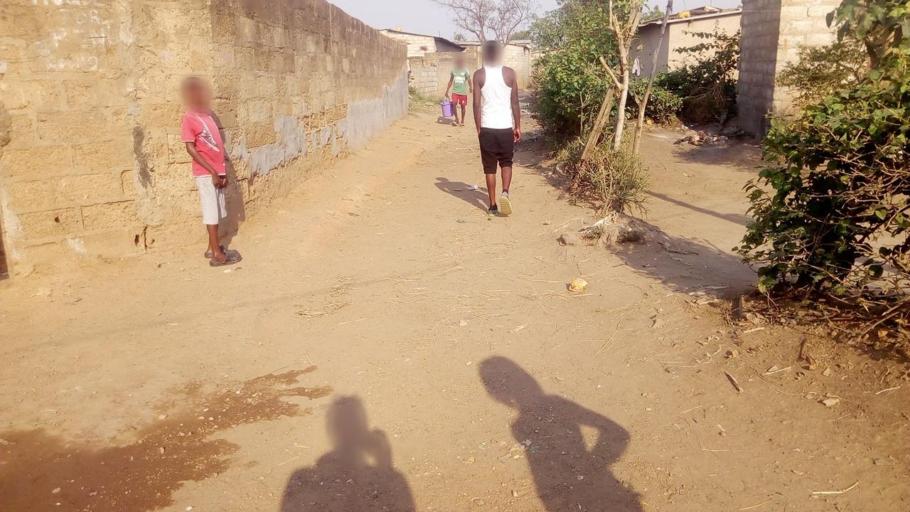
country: ZM
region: Lusaka
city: Lusaka
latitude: -15.3630
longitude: 28.3009
